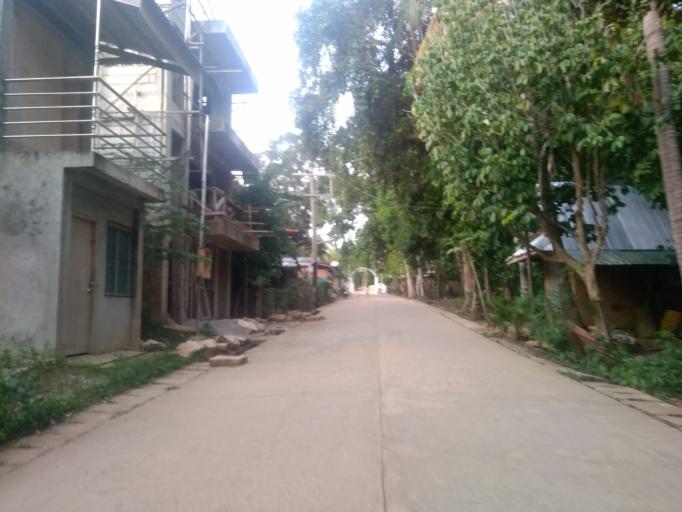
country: PH
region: Central Visayas
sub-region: Province of Siquijor
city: Lazi
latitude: 9.1306
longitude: 123.6332
